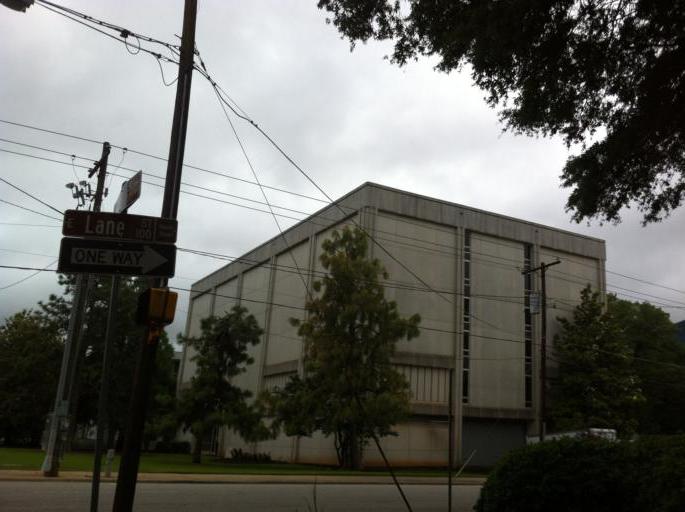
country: US
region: North Carolina
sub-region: Wake County
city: Raleigh
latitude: 35.7839
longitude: -78.6364
